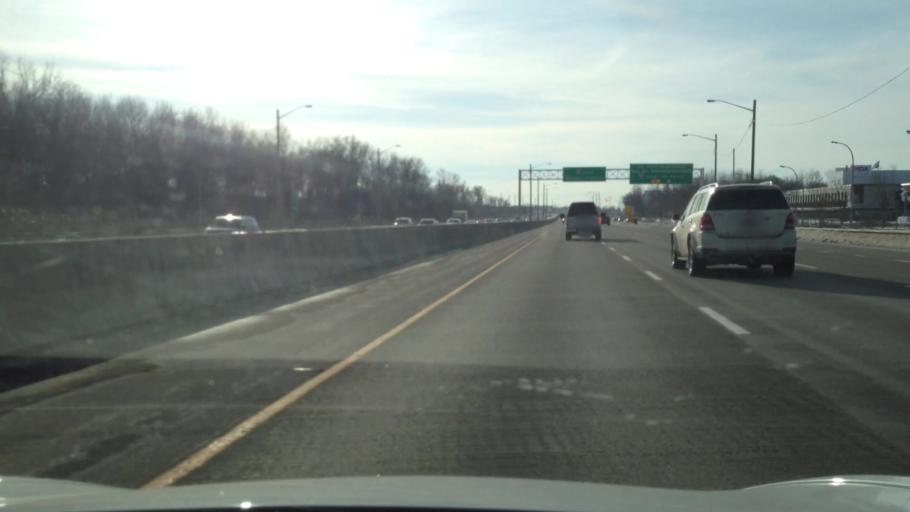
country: CA
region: Quebec
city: Baie-D'Urfe
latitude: 45.4244
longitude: -73.9224
